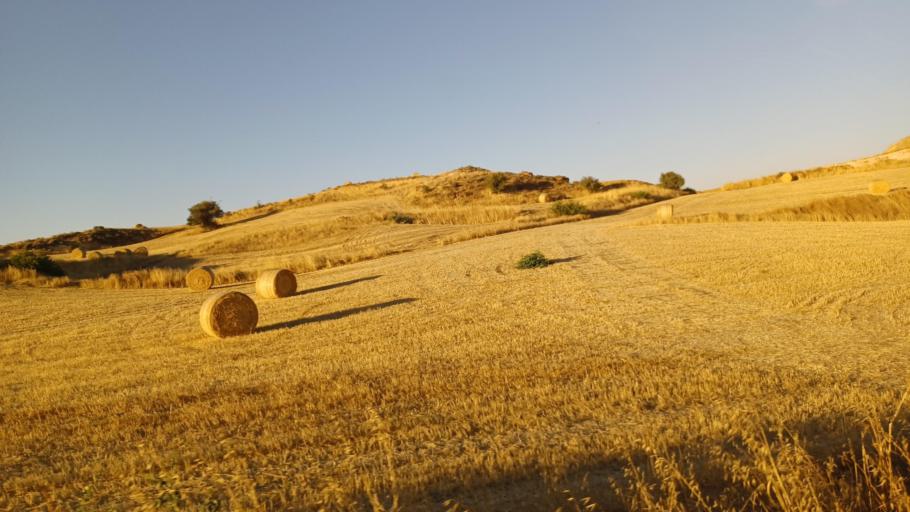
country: CY
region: Larnaka
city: Troulloi
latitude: 35.0296
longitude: 33.6425
